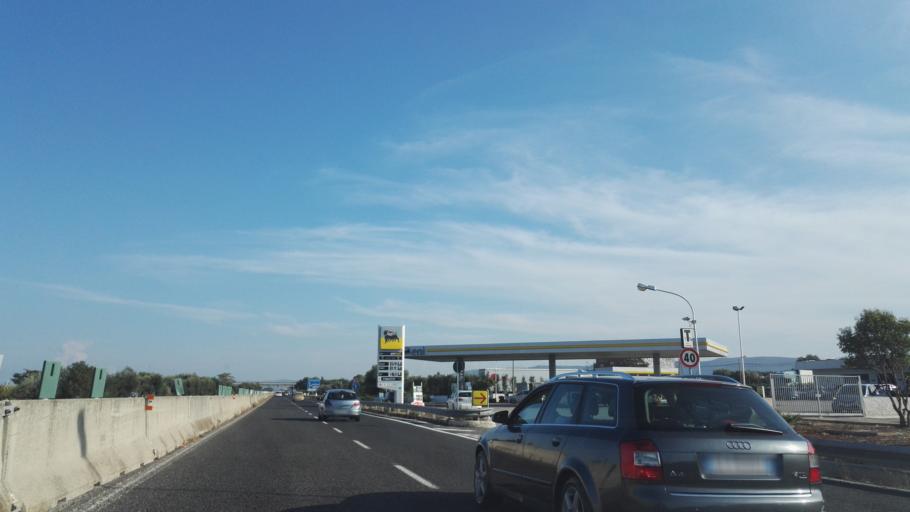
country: IT
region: Apulia
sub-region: Provincia di Bari
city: Monopoli
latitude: 40.9112
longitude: 17.3218
